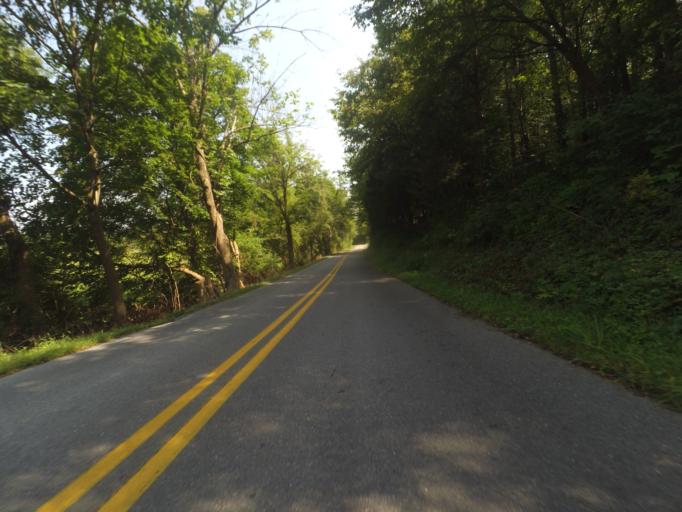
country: US
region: Pennsylvania
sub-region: Centre County
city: Bellefonte
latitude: 40.9012
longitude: -77.7821
